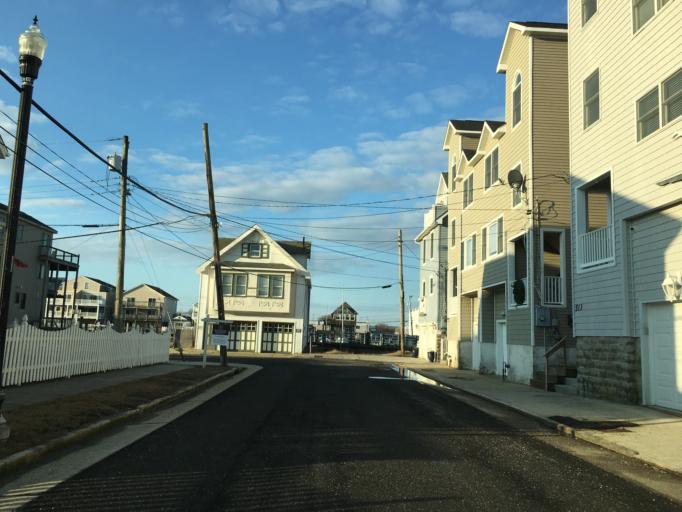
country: US
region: New Jersey
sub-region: Atlantic County
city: Atlantic City
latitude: 39.3749
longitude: -74.4235
